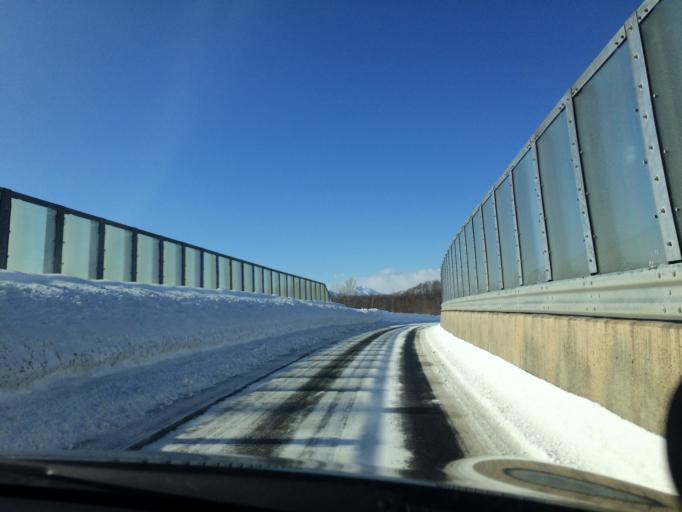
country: JP
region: Hokkaido
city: Chitose
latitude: 42.8455
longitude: 141.5851
